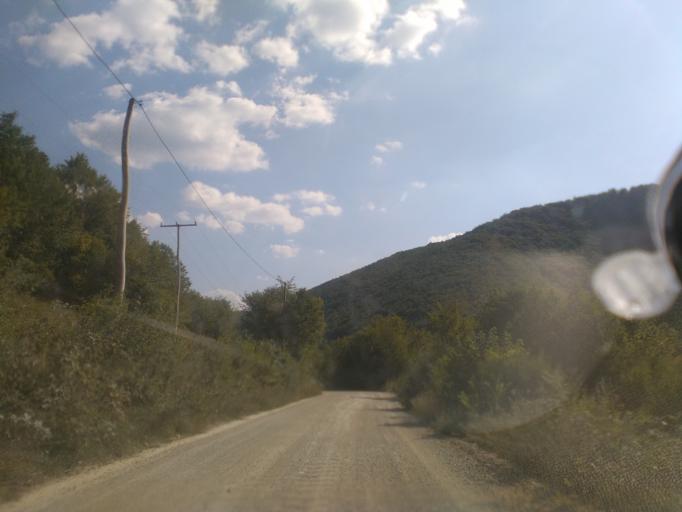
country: BA
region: Federation of Bosnia and Herzegovina
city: Orasac
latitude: 44.5126
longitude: 16.1277
